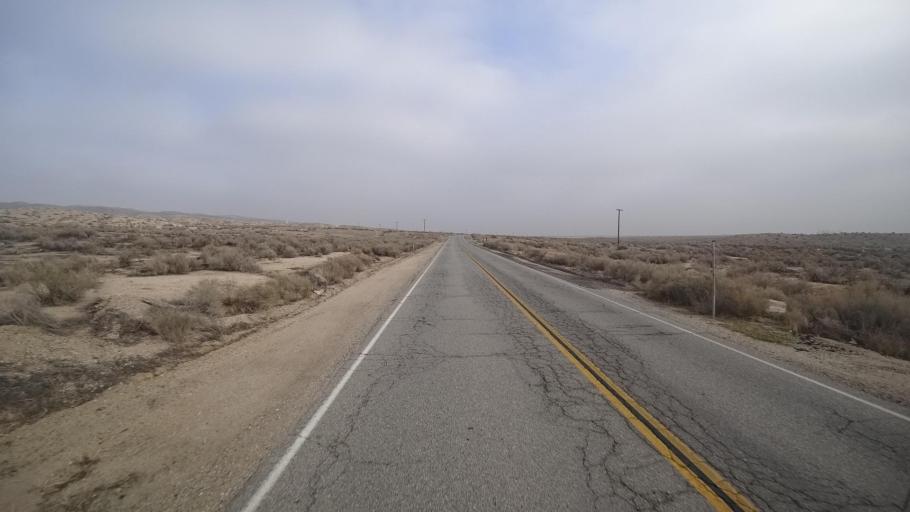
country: US
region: California
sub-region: Kern County
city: South Taft
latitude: 35.1363
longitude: -119.4101
